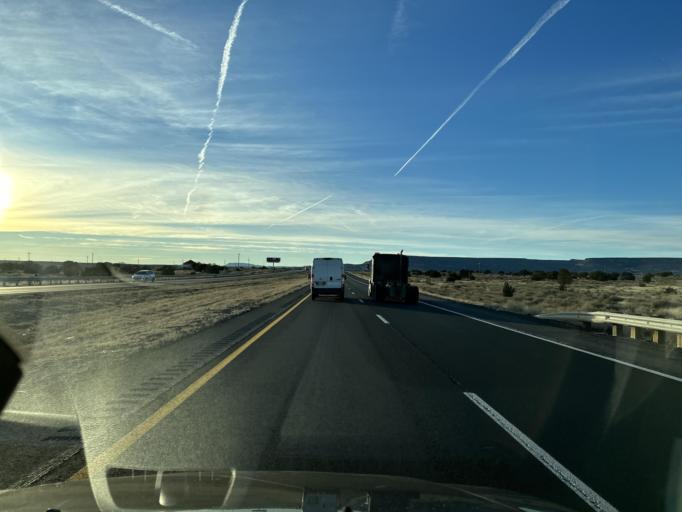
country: US
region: New Mexico
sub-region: Cibola County
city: Skyline-Ganipa
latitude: 35.0757
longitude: -107.6000
